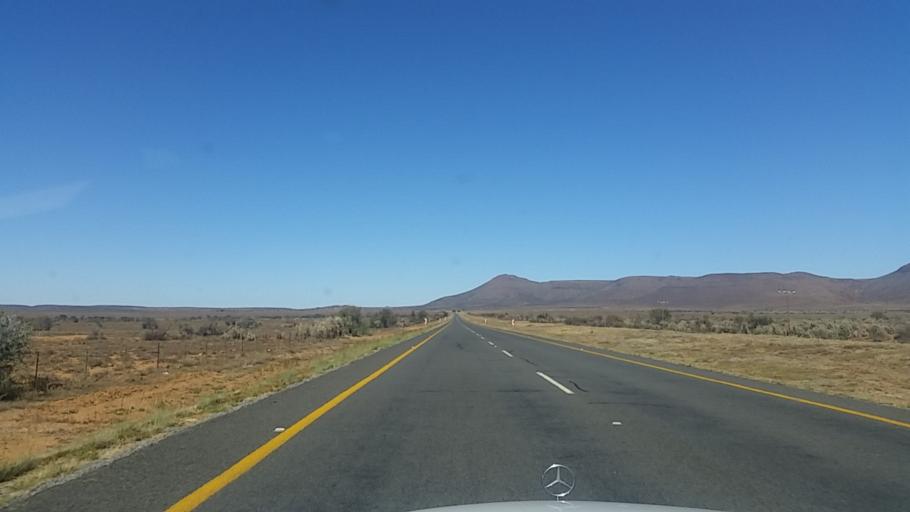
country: ZA
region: Eastern Cape
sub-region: Cacadu District Municipality
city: Graaff-Reinet
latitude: -32.0077
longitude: 24.6567
